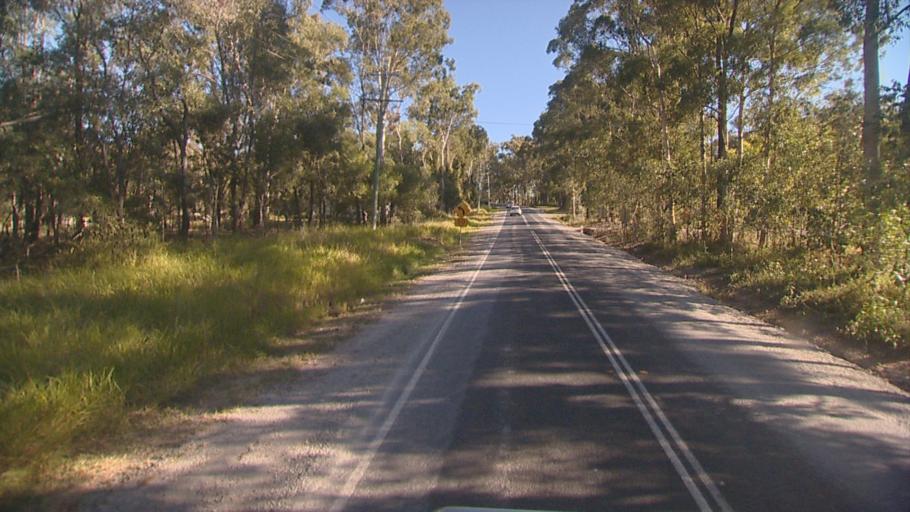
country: AU
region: Queensland
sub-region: Logan
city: Waterford West
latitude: -27.7408
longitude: 153.1451
